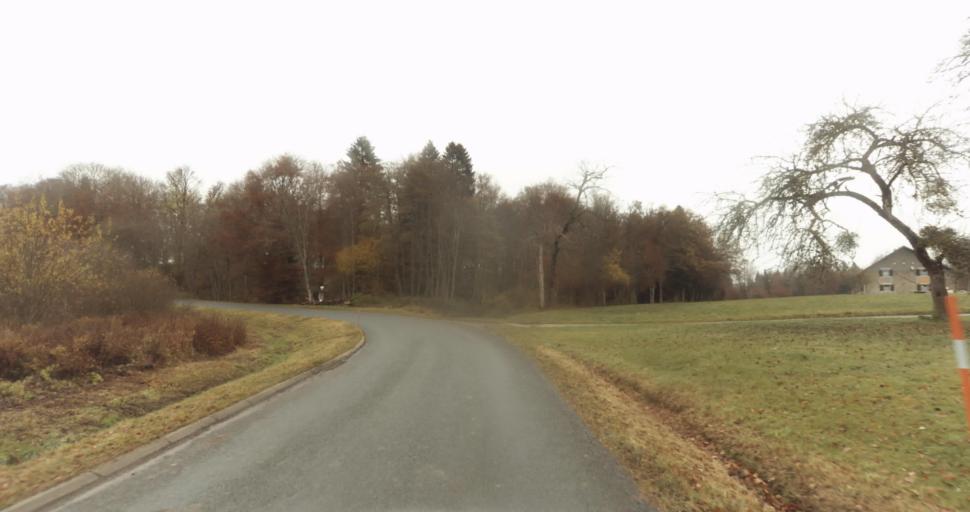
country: FR
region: Rhone-Alpes
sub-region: Departement de la Haute-Savoie
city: Evires
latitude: 46.0659
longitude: 6.2124
